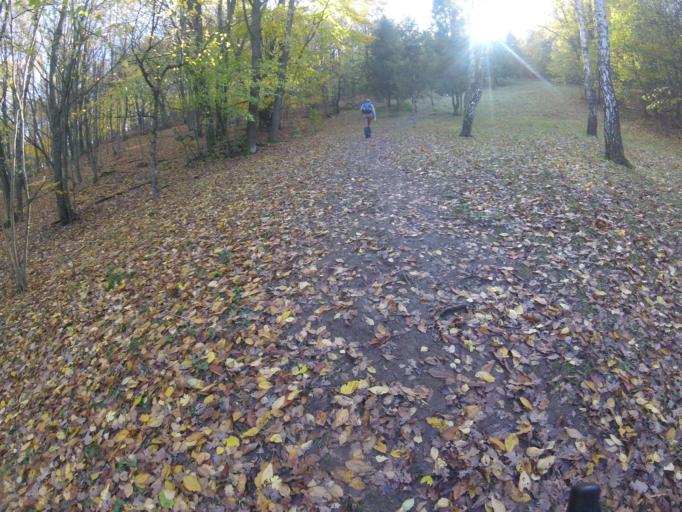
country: HU
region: Borsod-Abauj-Zemplen
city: Tolcsva
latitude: 48.3756
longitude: 21.3958
